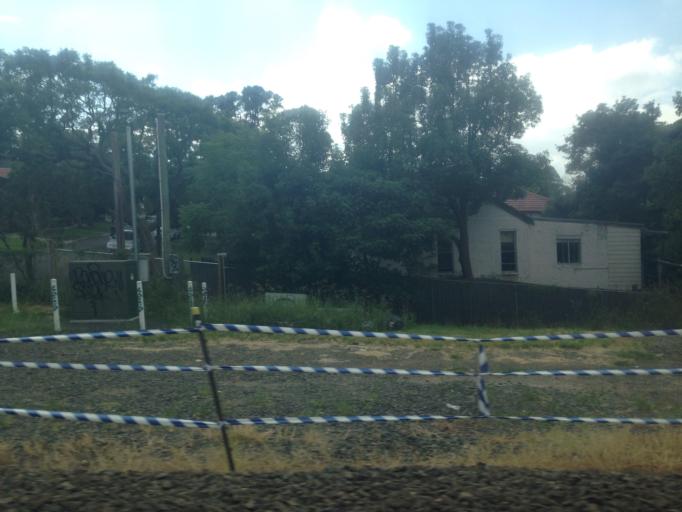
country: AU
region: New South Wales
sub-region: Willoughby
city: Chatswood
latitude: -33.8060
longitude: 151.1823
